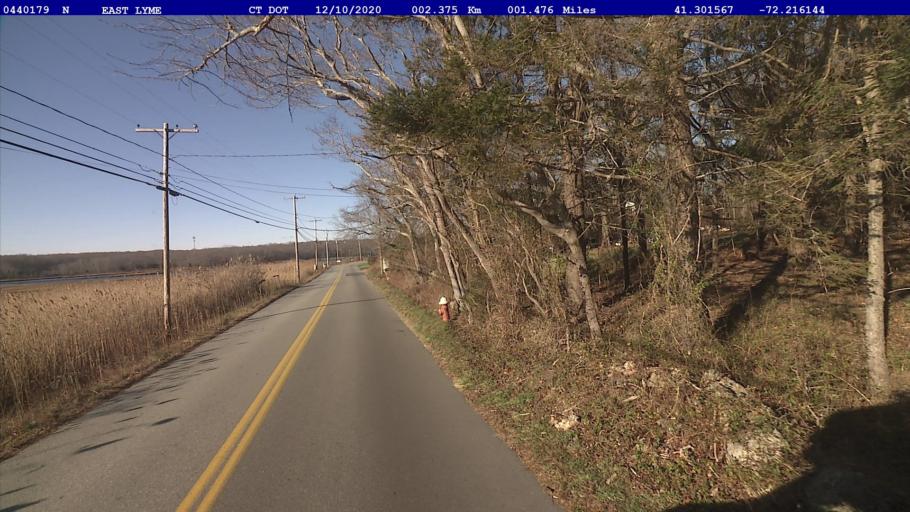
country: US
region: Connecticut
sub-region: New London County
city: Niantic
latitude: 41.3018
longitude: -72.2162
